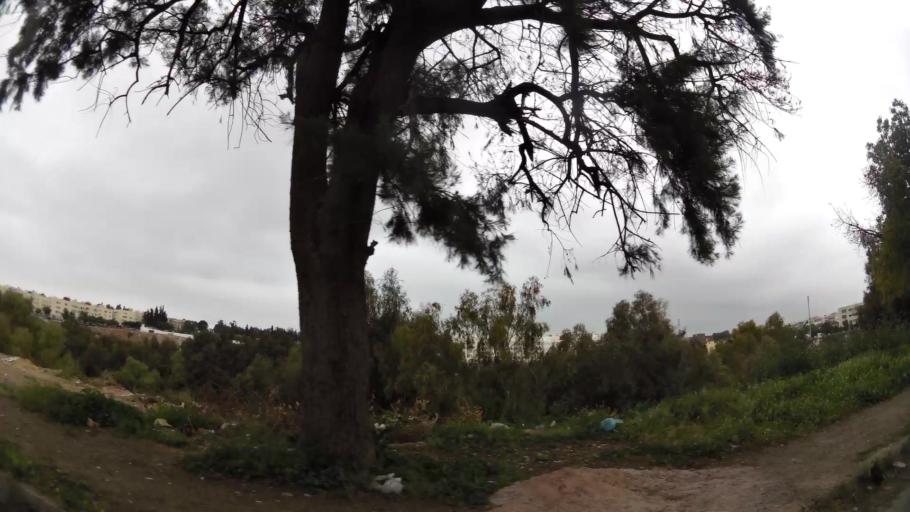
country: MA
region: Fes-Boulemane
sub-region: Fes
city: Fes
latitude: 34.0380
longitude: -4.9923
